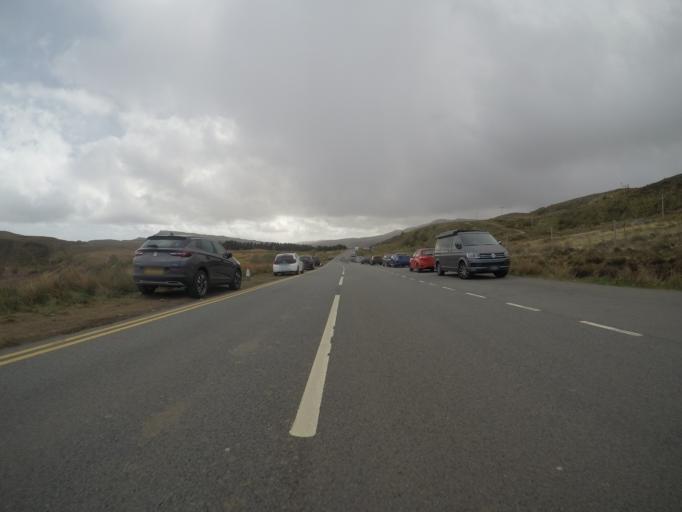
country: GB
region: Scotland
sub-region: Highland
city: Portree
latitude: 57.4995
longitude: -6.1572
